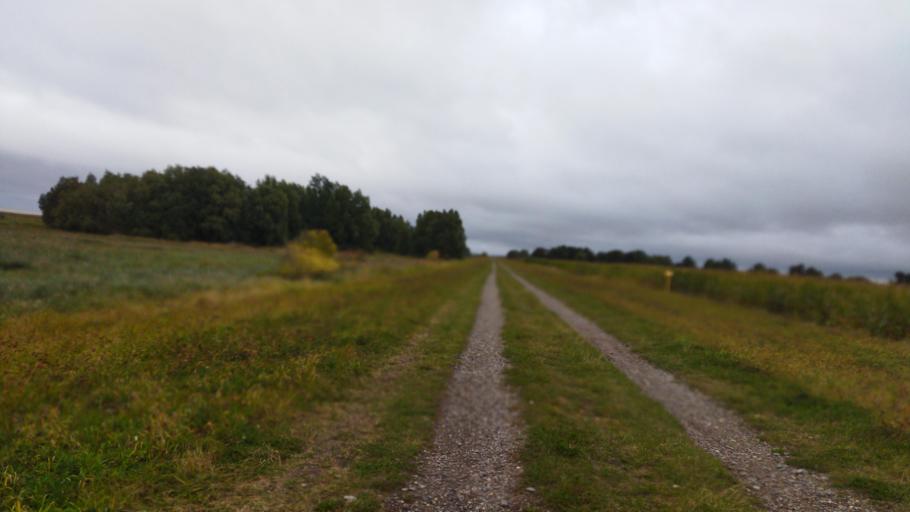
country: NL
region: Groningen
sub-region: Gemeente Delfzijl
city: Delfzijl
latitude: 53.3681
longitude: 7.0054
